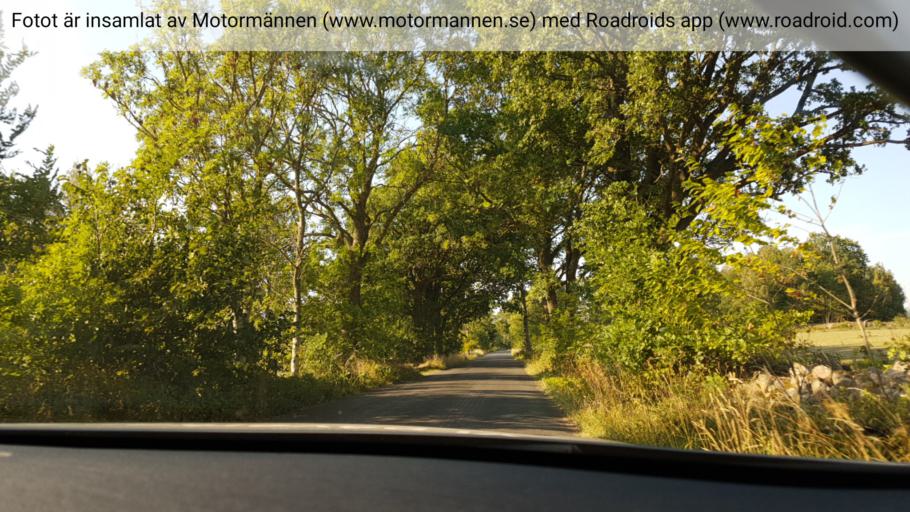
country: SE
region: Vaestra Goetaland
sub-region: Skovde Kommun
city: Stopen
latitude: 58.5150
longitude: 13.7831
